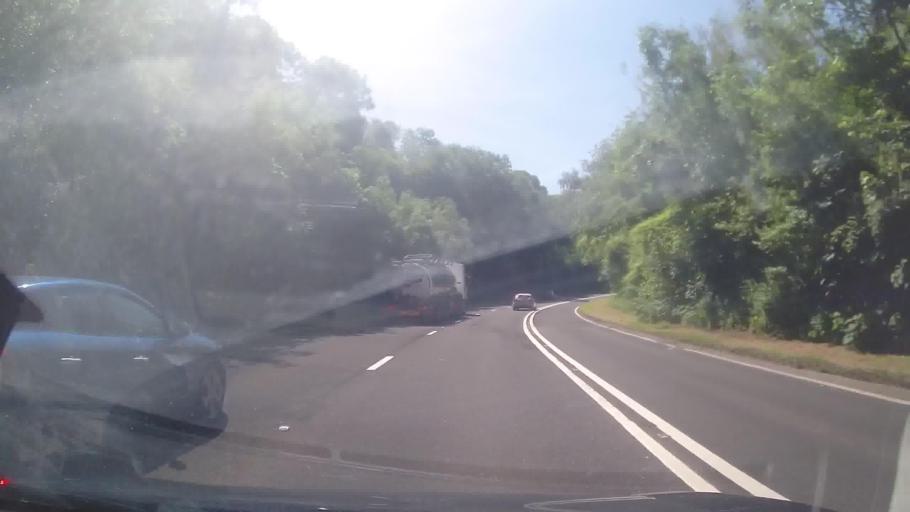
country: GB
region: England
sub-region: Herefordshire
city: Hope under Dinmore
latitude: 52.1648
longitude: -2.7191
